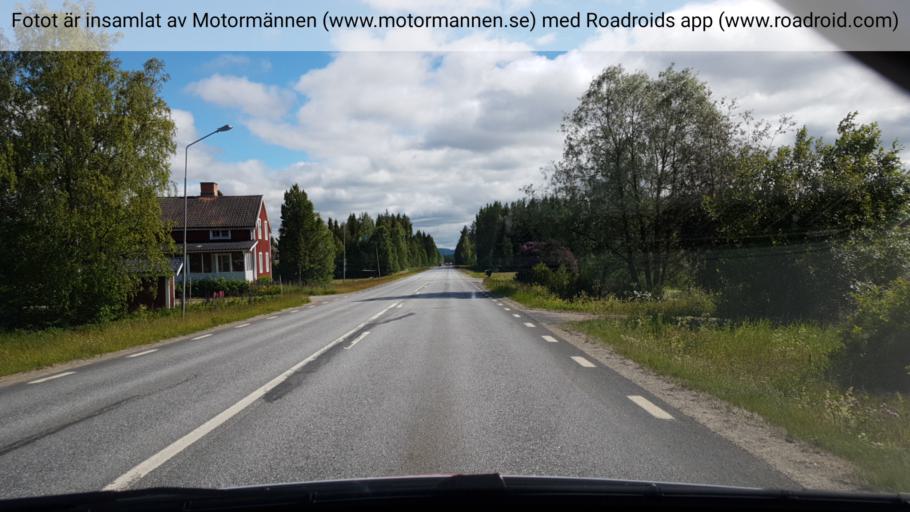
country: SE
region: Vaesterbotten
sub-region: Vannas Kommun
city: Vaennaes
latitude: 63.9623
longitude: 19.7519
